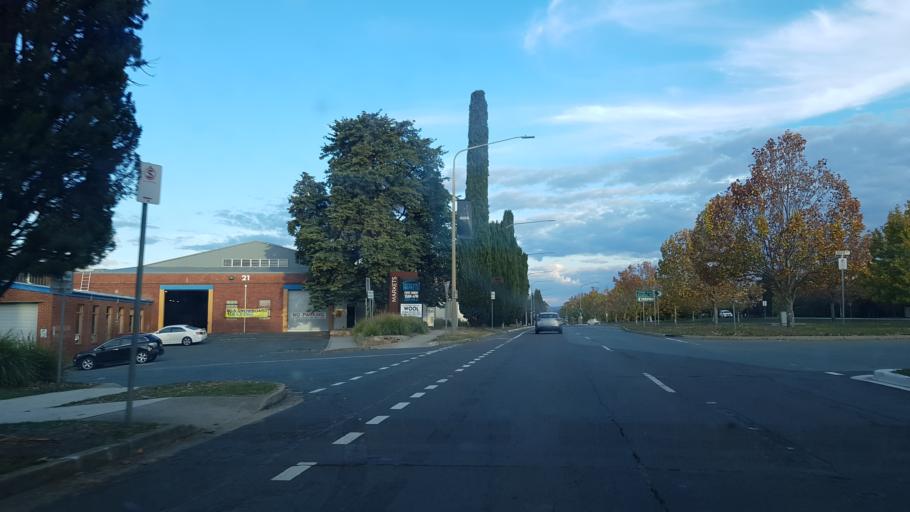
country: AU
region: Australian Capital Territory
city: Forrest
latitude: -35.3120
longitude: 149.1432
